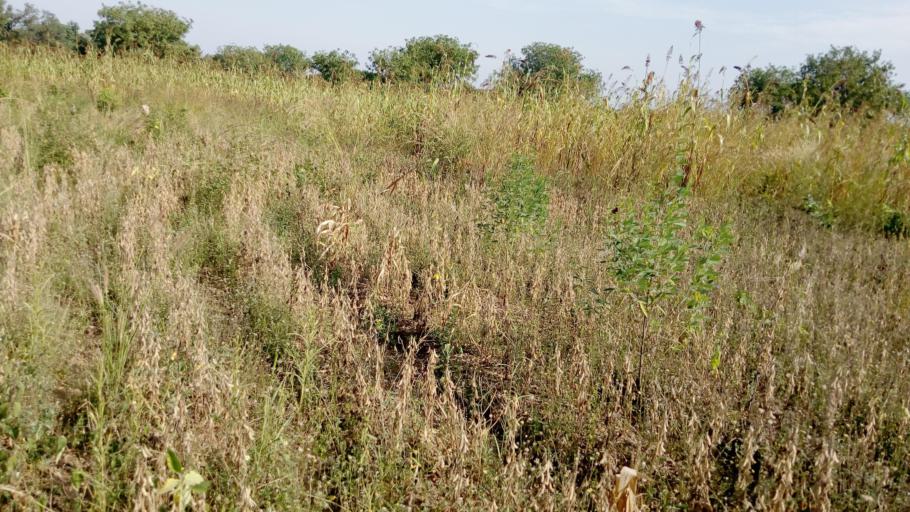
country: TG
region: Plateaux
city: Atakpame
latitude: 7.7373
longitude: 1.0964
